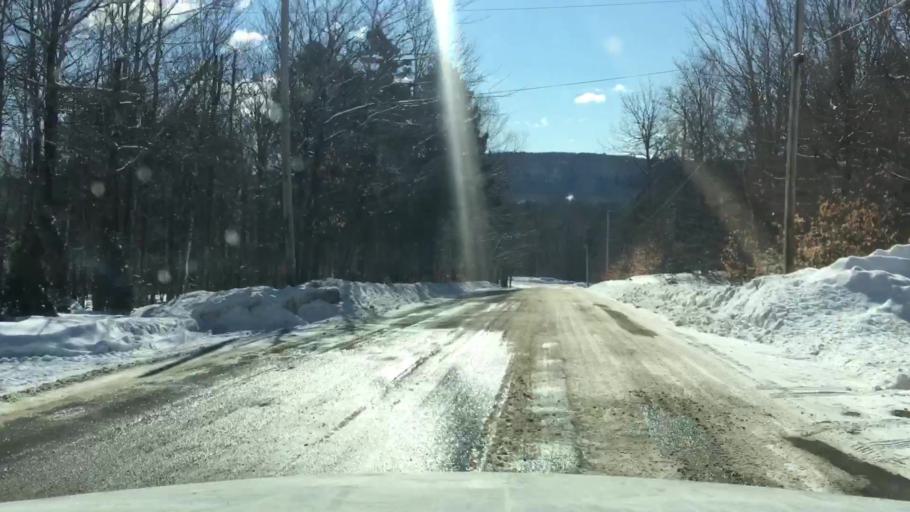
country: US
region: Maine
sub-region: Washington County
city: Calais
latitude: 45.0727
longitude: -67.5002
